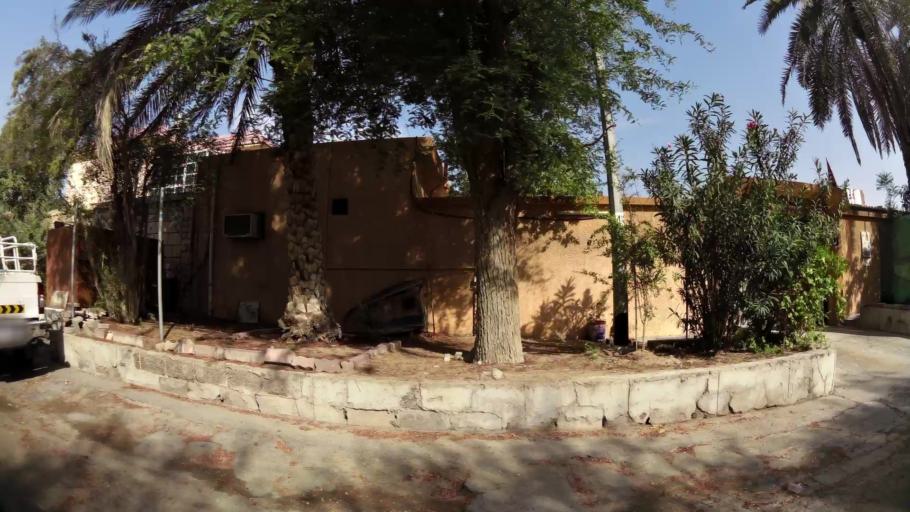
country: AE
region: Ash Shariqah
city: Sharjah
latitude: 25.2192
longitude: 55.3921
